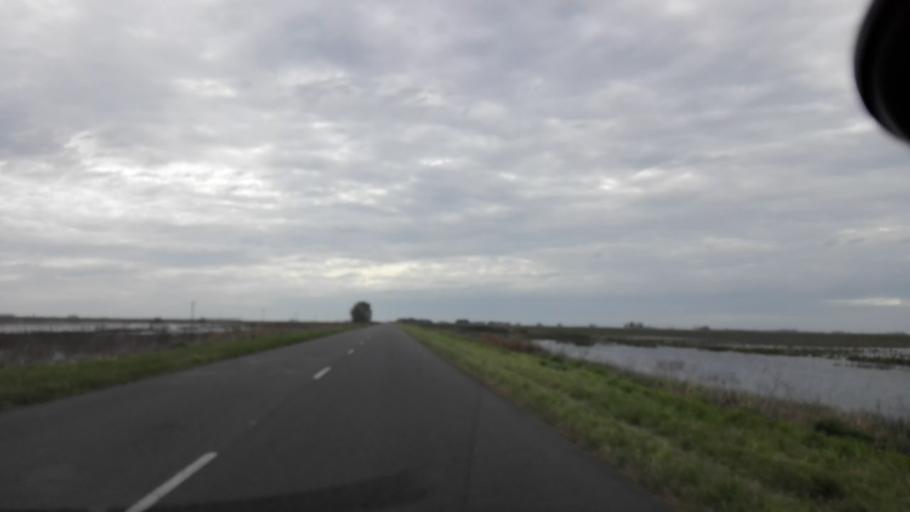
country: AR
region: Buenos Aires
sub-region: Partido de Las Flores
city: Las Flores
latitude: -36.3640
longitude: -59.0063
